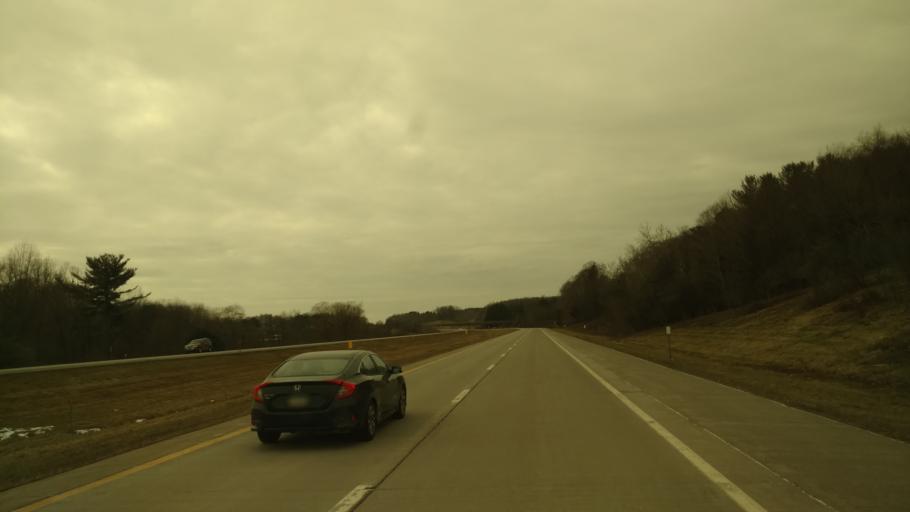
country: US
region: New York
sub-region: Chautauqua County
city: Lakewood
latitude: 42.1525
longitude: -79.4169
